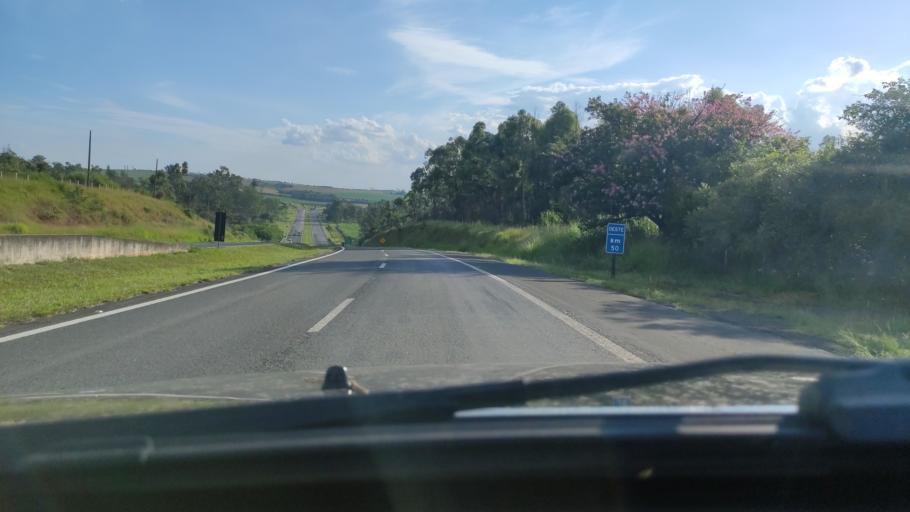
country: BR
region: Sao Paulo
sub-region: Itapira
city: Itapira
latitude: -22.4484
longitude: -46.8865
